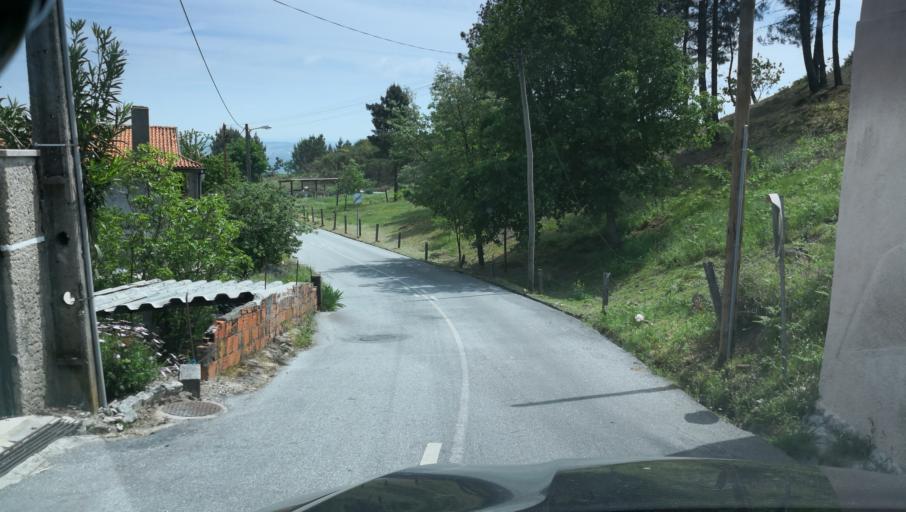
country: PT
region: Vila Real
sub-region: Vila Real
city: Vila Real
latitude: 41.3129
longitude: -7.7854
